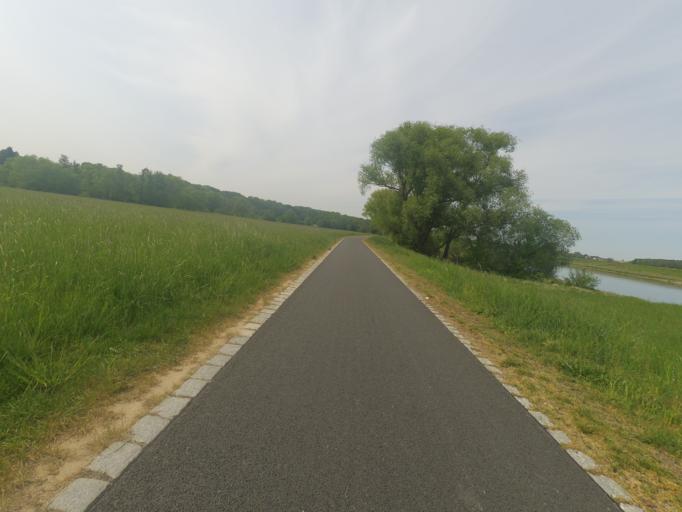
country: DE
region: Saxony
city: Strehla
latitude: 51.3545
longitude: 13.2343
